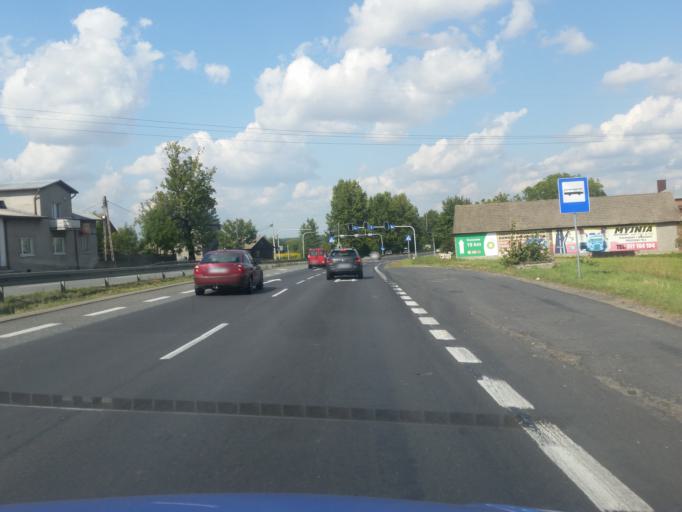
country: PL
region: Silesian Voivodeship
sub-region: Powiat bedzinski
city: Siewierz
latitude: 50.5051
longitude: 19.1978
